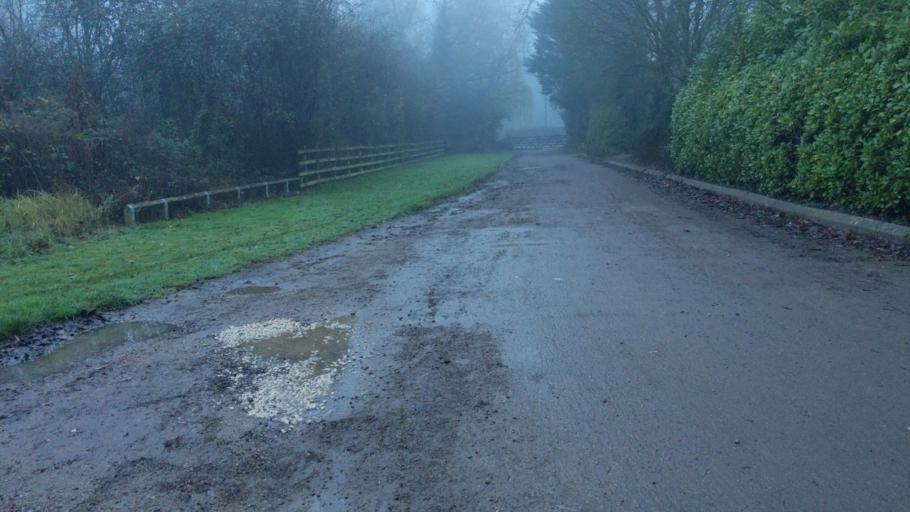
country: GB
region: England
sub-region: Milton Keynes
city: Water Eaton
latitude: 51.9981
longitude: -0.7100
